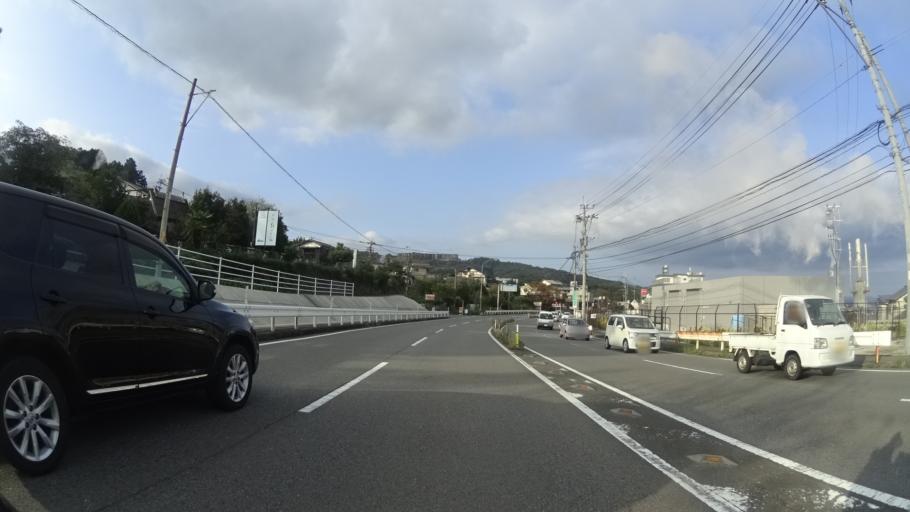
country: JP
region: Oita
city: Beppu
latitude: 33.3055
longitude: 131.4614
